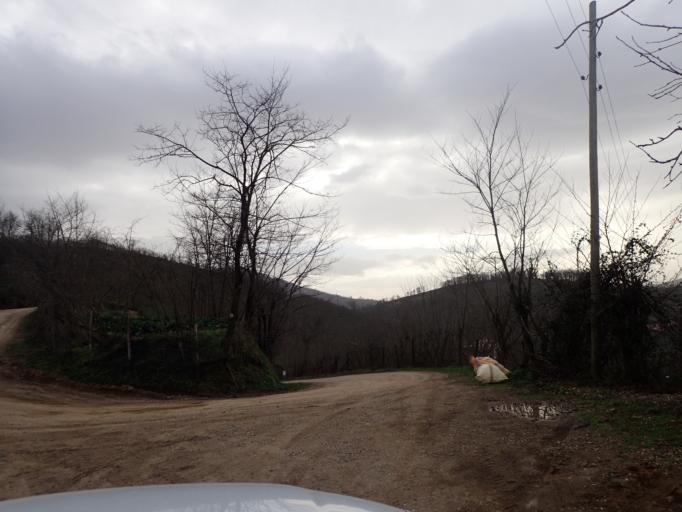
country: TR
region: Ordu
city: Camas
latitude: 40.8900
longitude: 37.4985
